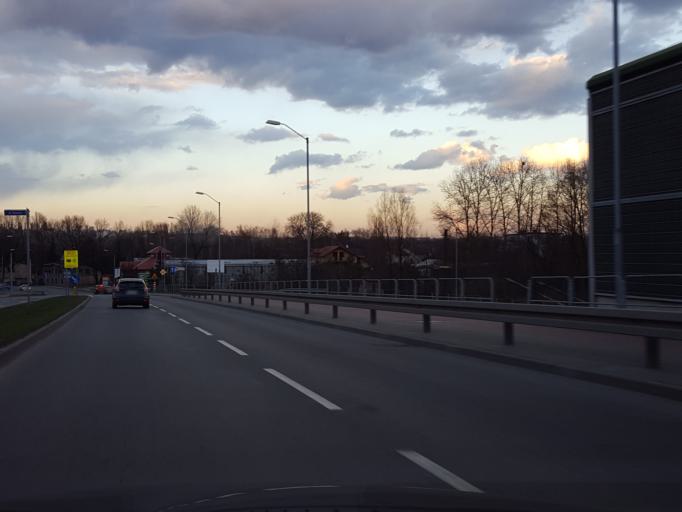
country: PL
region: Silesian Voivodeship
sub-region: Ruda Slaska
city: Ruda Slaska
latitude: 50.2564
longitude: 18.8564
